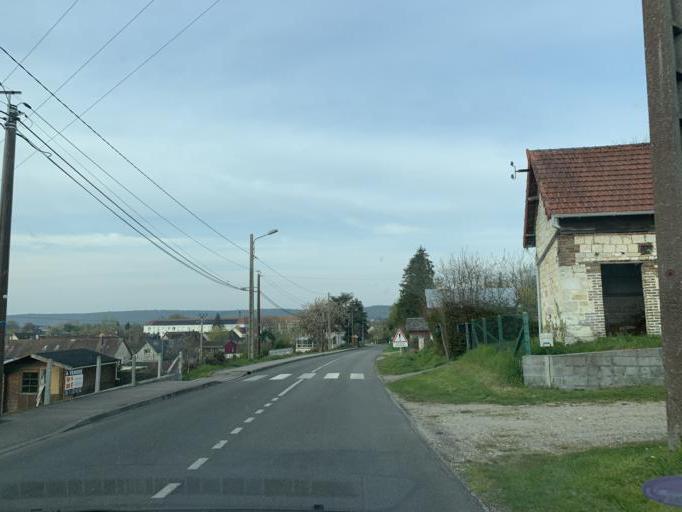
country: FR
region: Haute-Normandie
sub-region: Departement de la Seine-Maritime
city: La Mailleraye-sur-Seine
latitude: 49.4761
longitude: 0.7730
